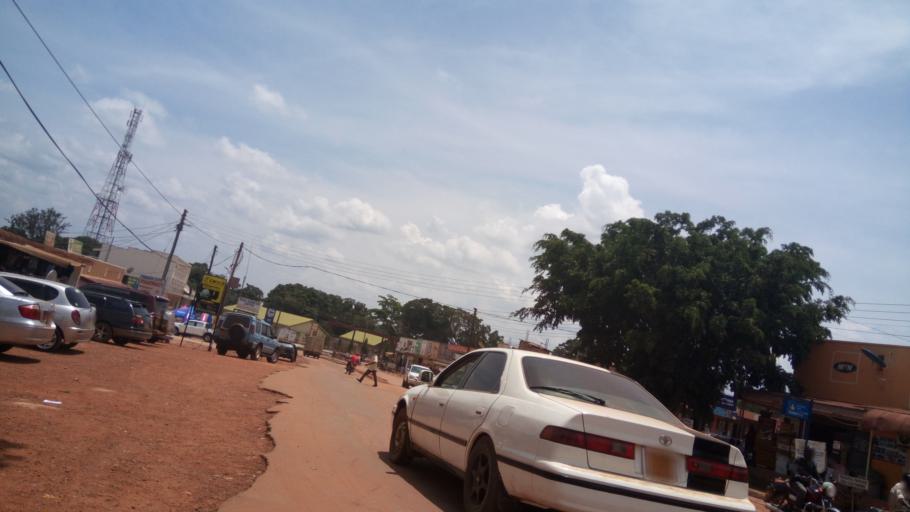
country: UG
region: Central Region
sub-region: Mityana District
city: Mityana
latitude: 0.4001
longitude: 32.0422
